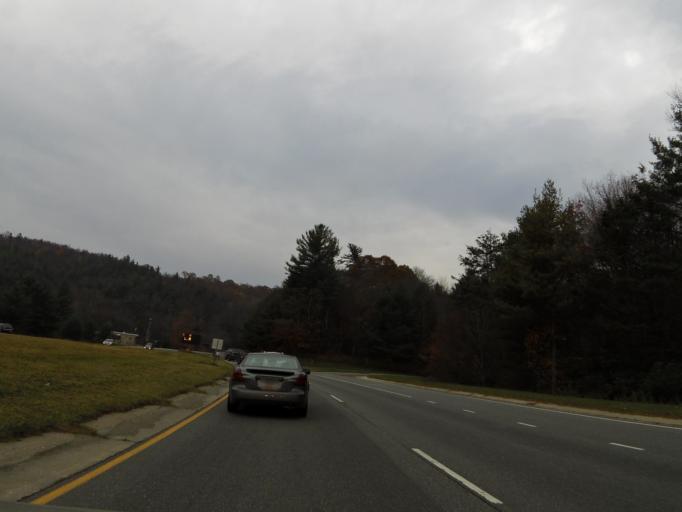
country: US
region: North Carolina
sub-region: Watauga County
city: Blowing Rock
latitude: 36.1476
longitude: -81.6631
